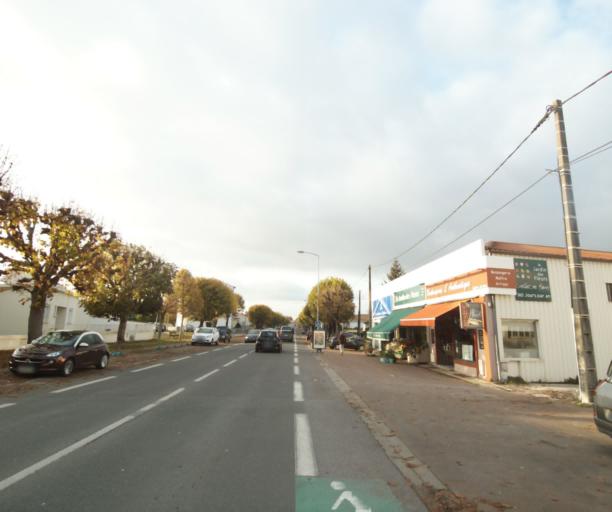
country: FR
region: Poitou-Charentes
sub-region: Departement de la Charente-Maritime
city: Saintes
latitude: 45.7494
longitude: -0.6457
